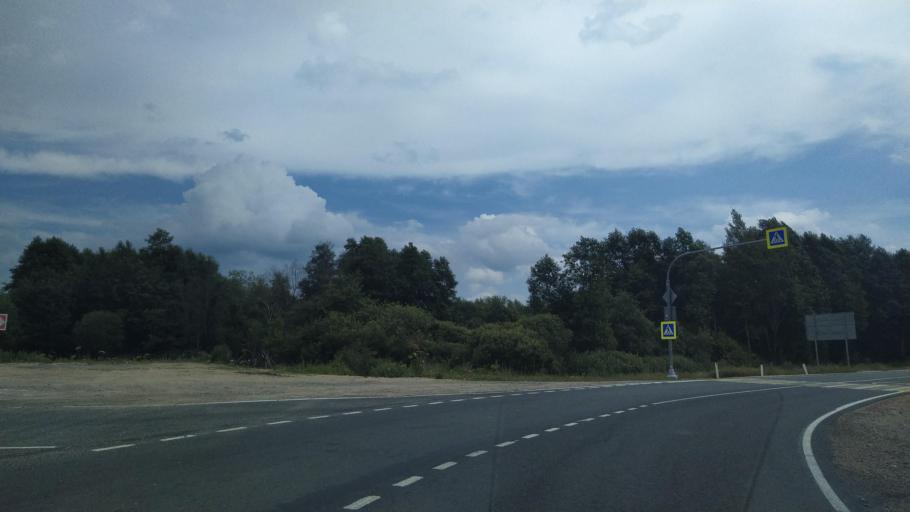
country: RU
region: Pskov
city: Pskov
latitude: 57.8144
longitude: 28.6938
